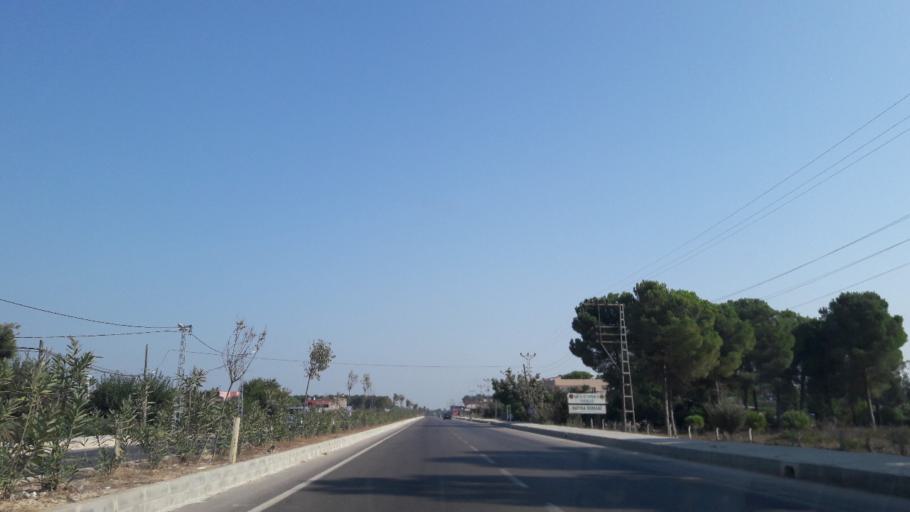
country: TR
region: Adana
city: Yakapinar
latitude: 37.1137
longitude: 35.5125
